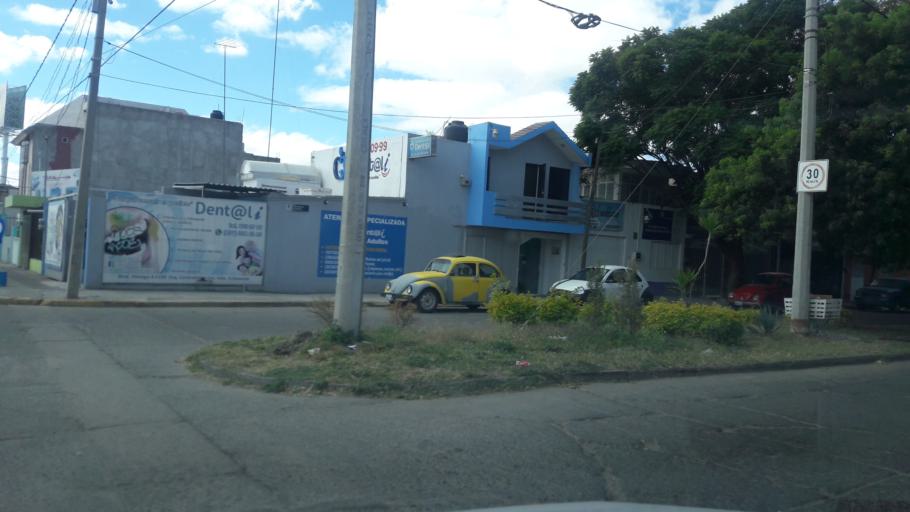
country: MX
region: Guanajuato
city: Leon
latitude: 21.1752
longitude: -101.6644
